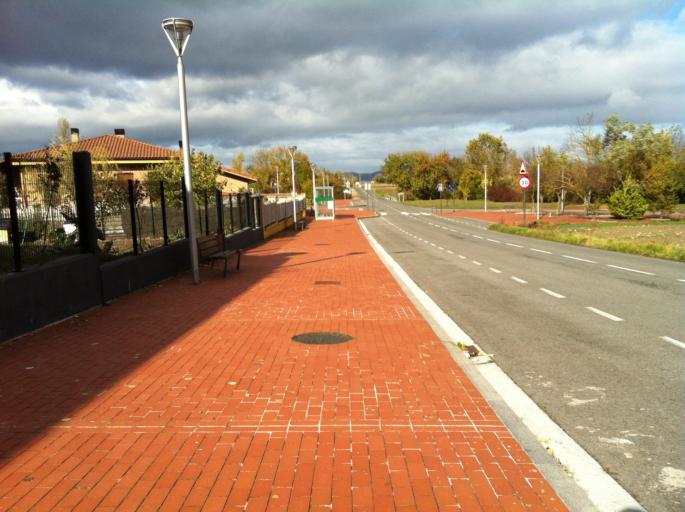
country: ES
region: Basque Country
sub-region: Provincia de Alava
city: Gasteiz / Vitoria
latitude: 42.8203
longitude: -2.6915
